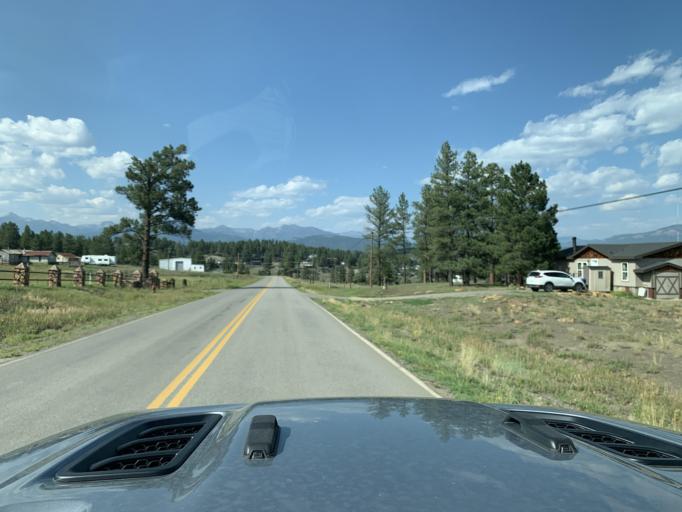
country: US
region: Colorado
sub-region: Archuleta County
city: Pagosa Springs
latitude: 37.2531
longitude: -107.0247
